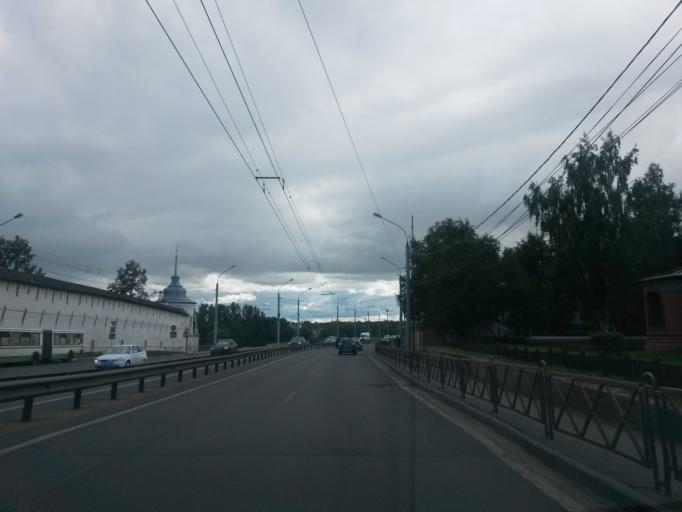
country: RU
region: Jaroslavl
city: Yaroslavl
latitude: 57.6218
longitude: 39.8869
